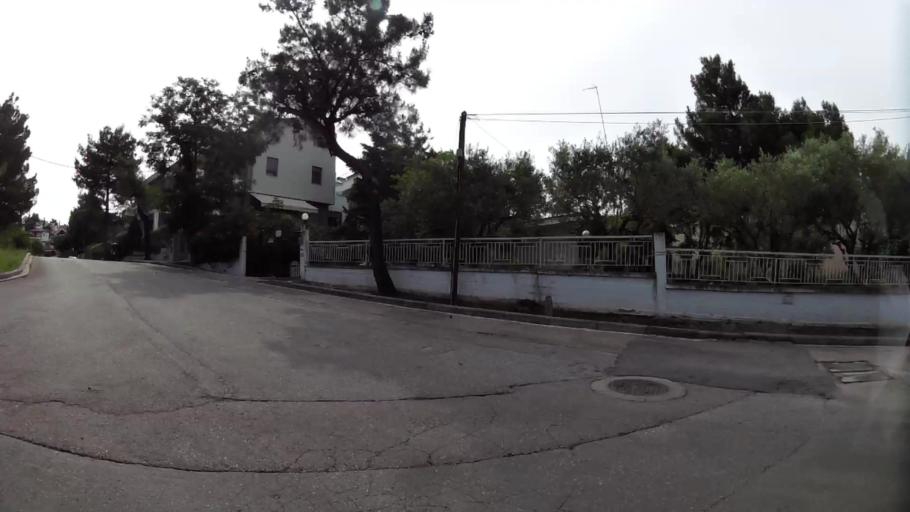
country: GR
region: Central Macedonia
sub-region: Nomos Thessalonikis
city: Panorama
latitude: 40.5879
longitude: 23.0161
